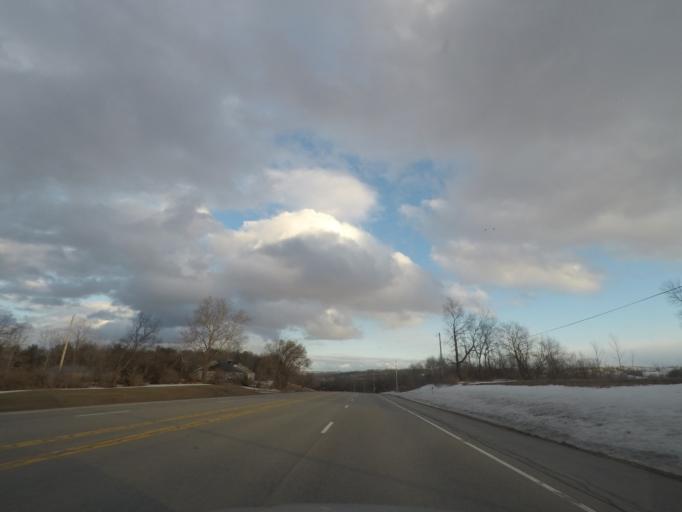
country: US
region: New York
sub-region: Herkimer County
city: Dolgeville
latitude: 43.0130
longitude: -74.7696
